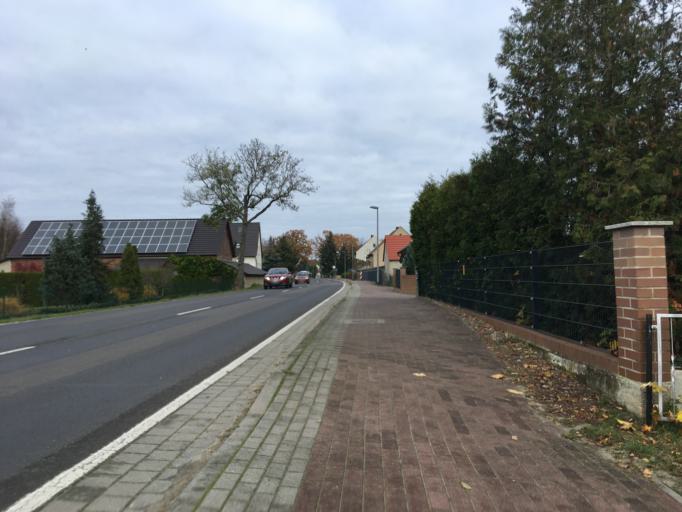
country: DE
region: Brandenburg
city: Peitz
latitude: 51.8676
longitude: 14.4180
